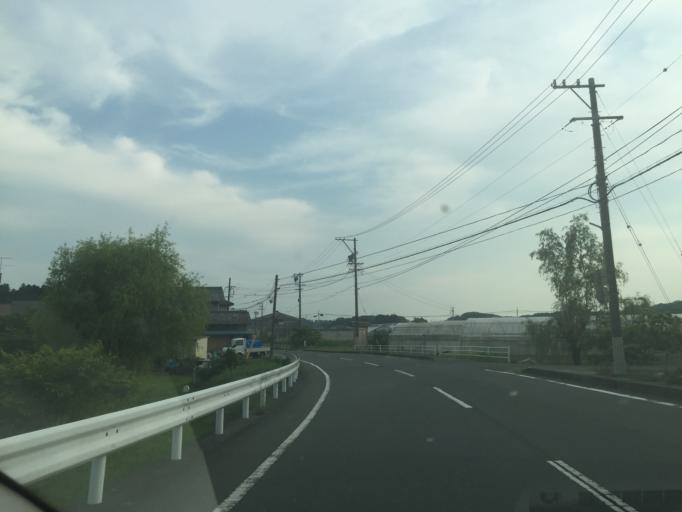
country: JP
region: Shizuoka
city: Kakegawa
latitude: 34.8124
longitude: 138.0144
